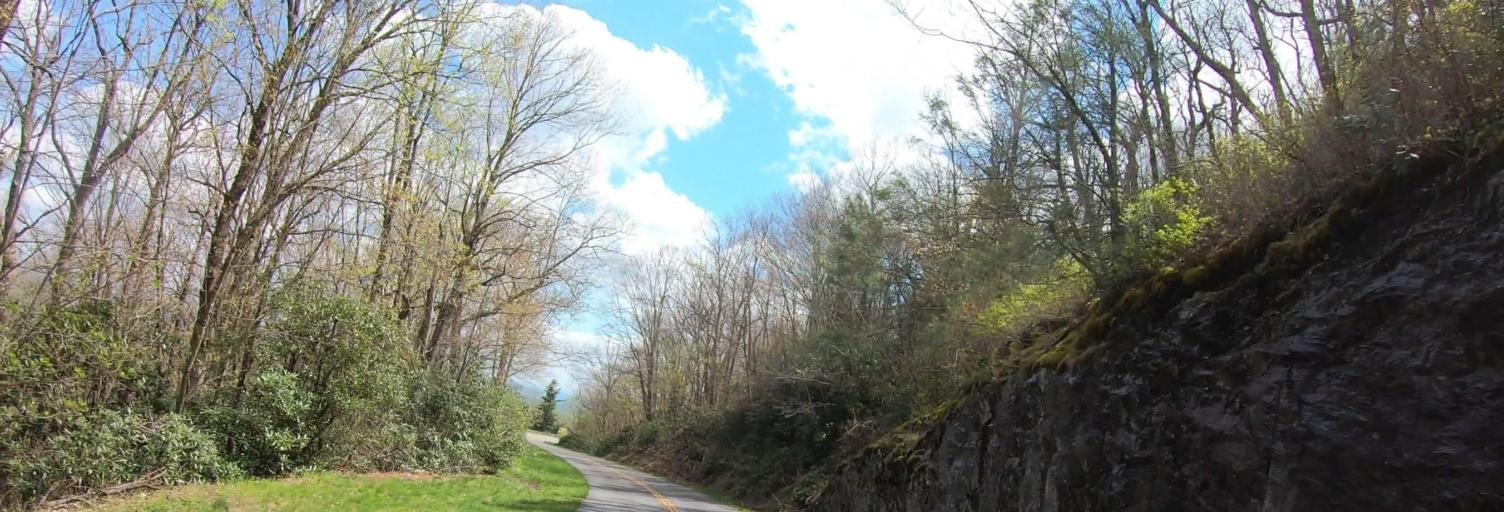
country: US
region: North Carolina
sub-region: Alleghany County
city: Sparta
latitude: 36.4441
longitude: -81.0894
